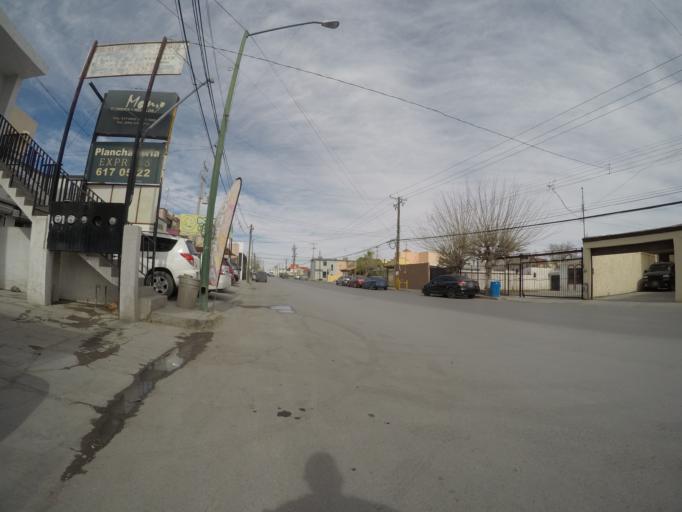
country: MX
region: Chihuahua
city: Ciudad Juarez
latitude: 31.7123
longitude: -106.4341
